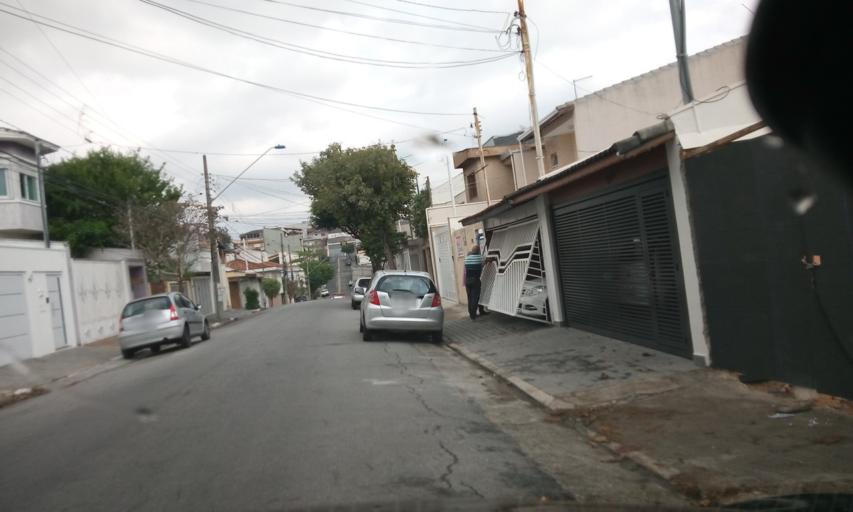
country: BR
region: Sao Paulo
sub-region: Sao Caetano Do Sul
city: Sao Caetano do Sul
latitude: -23.6249
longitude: -46.5704
